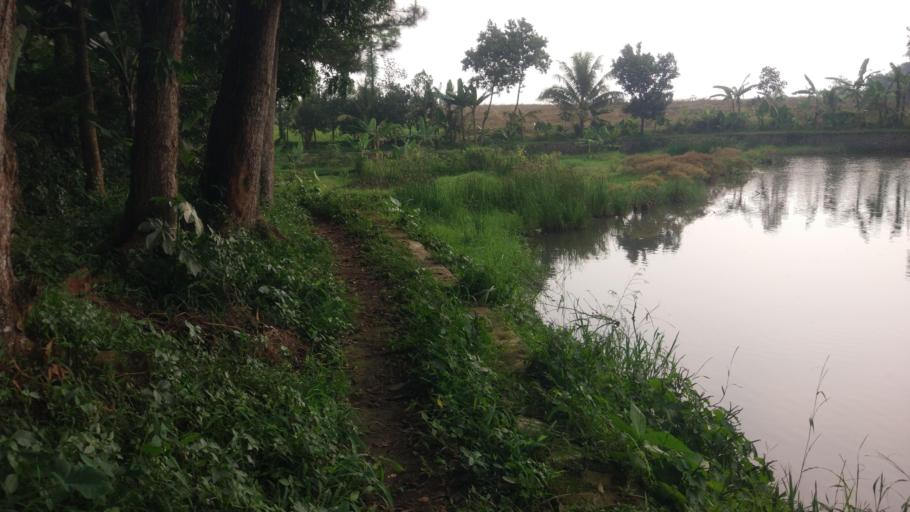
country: ID
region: West Java
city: Ciampea
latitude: -6.5340
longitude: 106.7293
